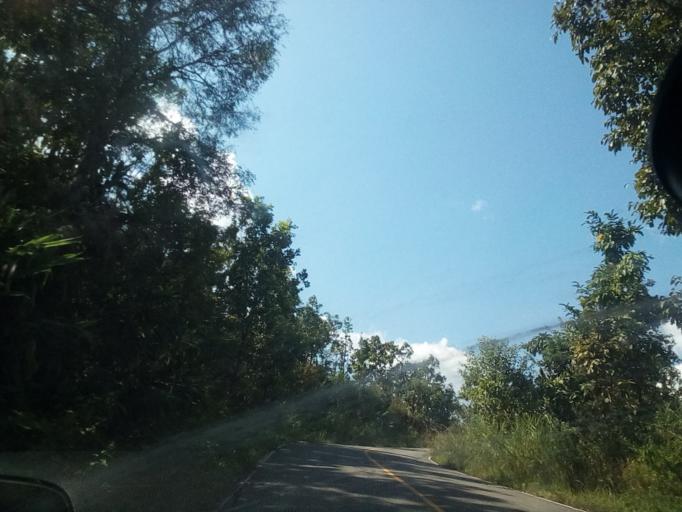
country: TH
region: Chiang Mai
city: Samoeng
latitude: 18.8686
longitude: 98.6928
